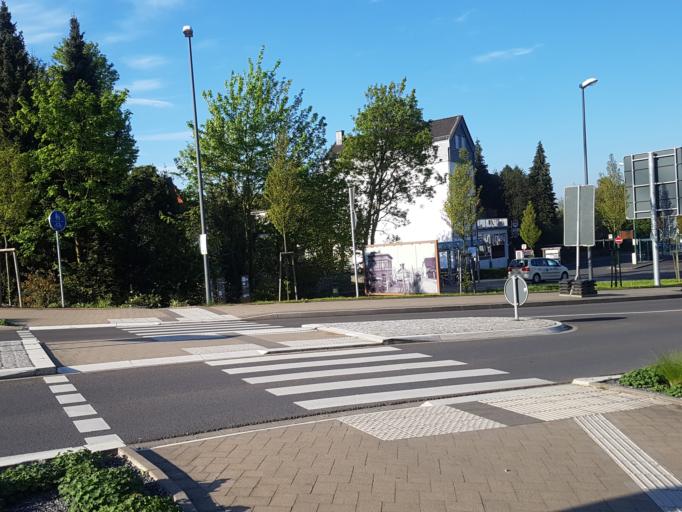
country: DE
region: North Rhine-Westphalia
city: Waldbrol
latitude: 50.8752
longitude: 7.6143
